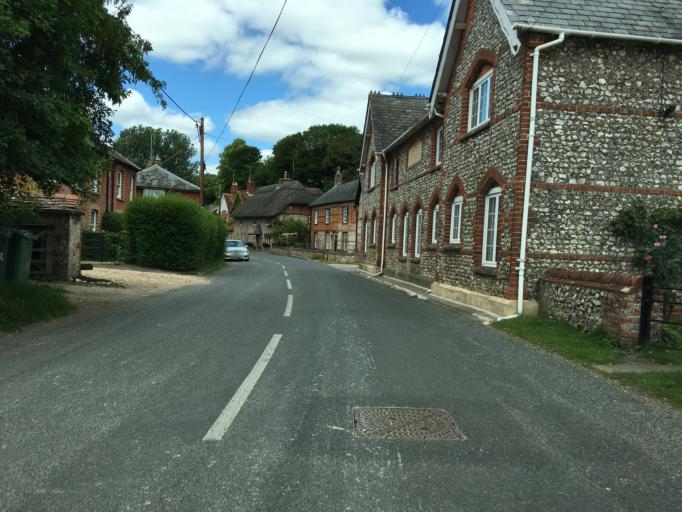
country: GB
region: England
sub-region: Hampshire
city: Highclere
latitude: 51.2515
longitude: -1.3970
